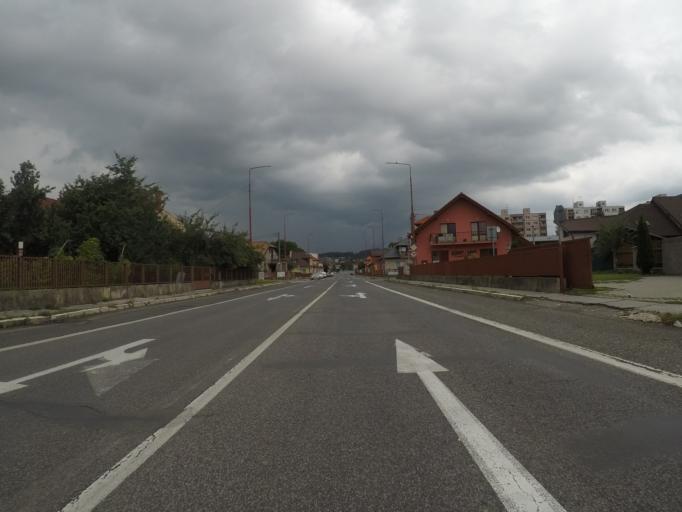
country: SK
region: Kosicky
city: Spisska Nova Ves
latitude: 48.9394
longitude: 20.5590
